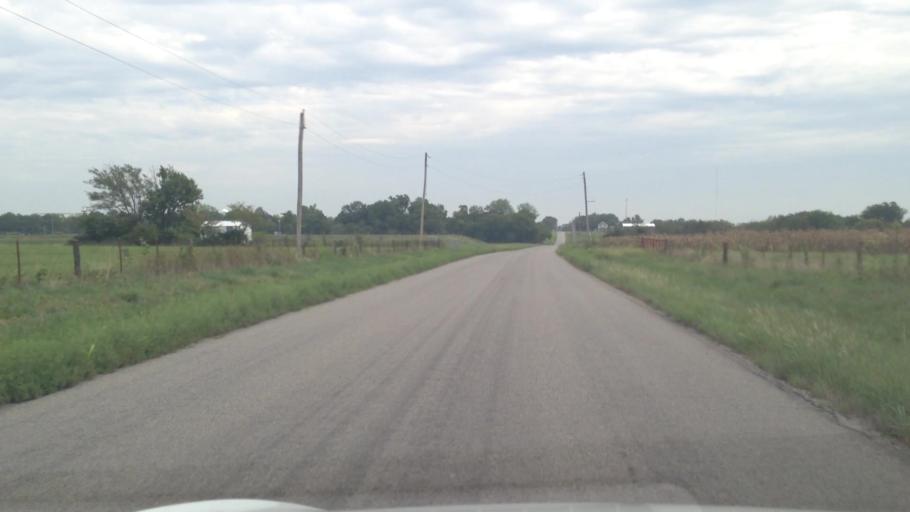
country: US
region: Kansas
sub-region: Crawford County
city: Girard
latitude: 37.4994
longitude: -94.8617
